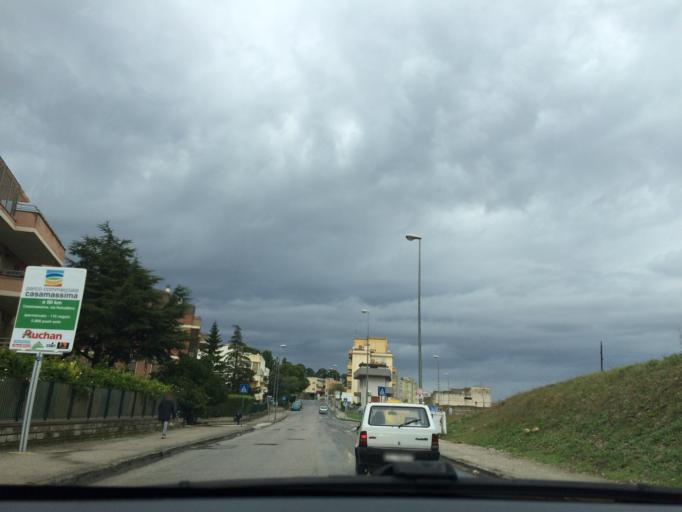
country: IT
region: Basilicate
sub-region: Provincia di Matera
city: Matera
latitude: 40.6547
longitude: 16.6174
